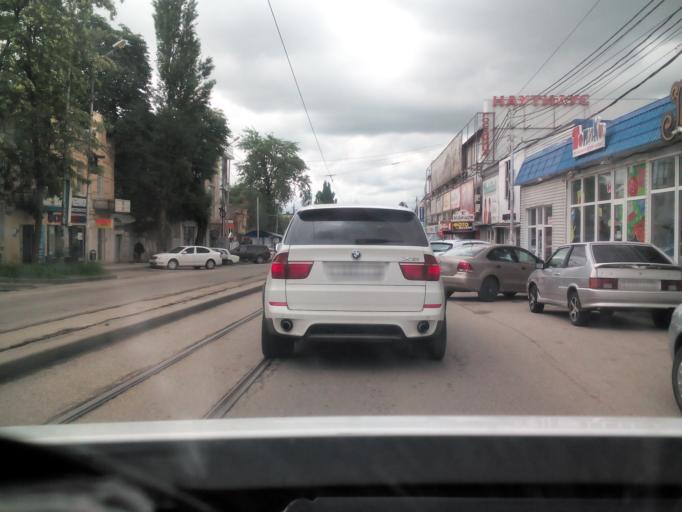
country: RU
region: Stavropol'skiy
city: Pyatigorsk
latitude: 44.0423
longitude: 43.0641
